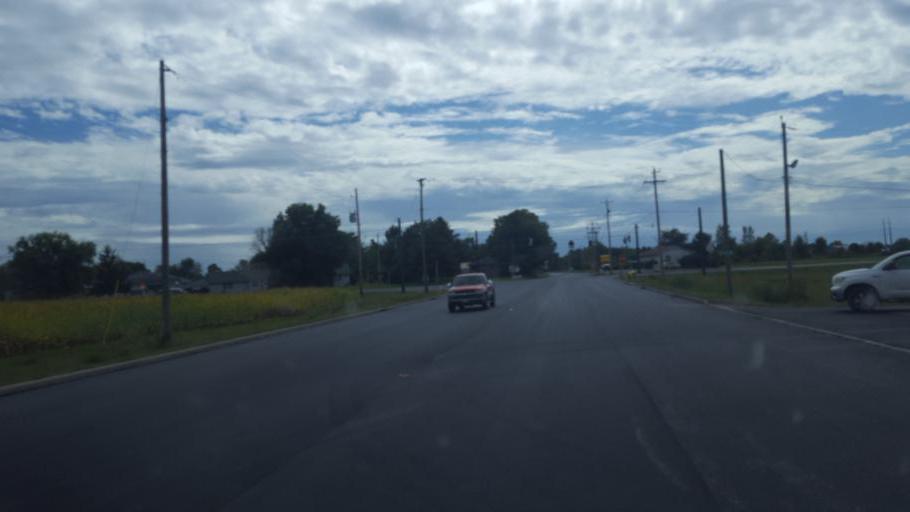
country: US
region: Ohio
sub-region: Licking County
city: Johnstown
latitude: 40.0790
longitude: -82.7234
